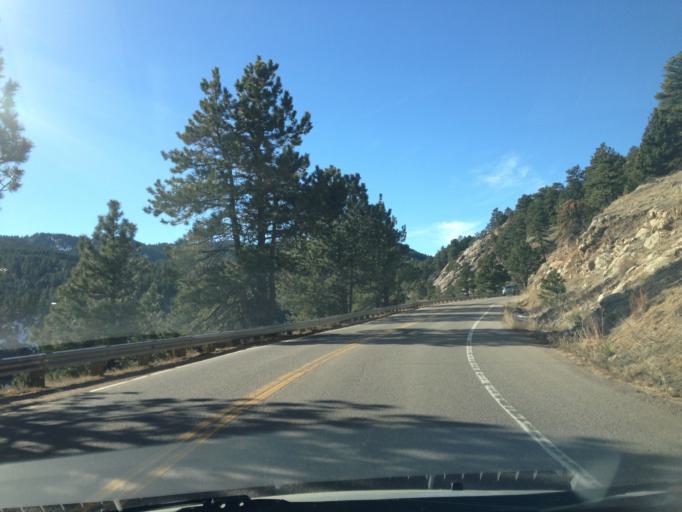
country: US
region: Colorado
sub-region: Boulder County
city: Boulder
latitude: 40.0003
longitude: -105.3024
